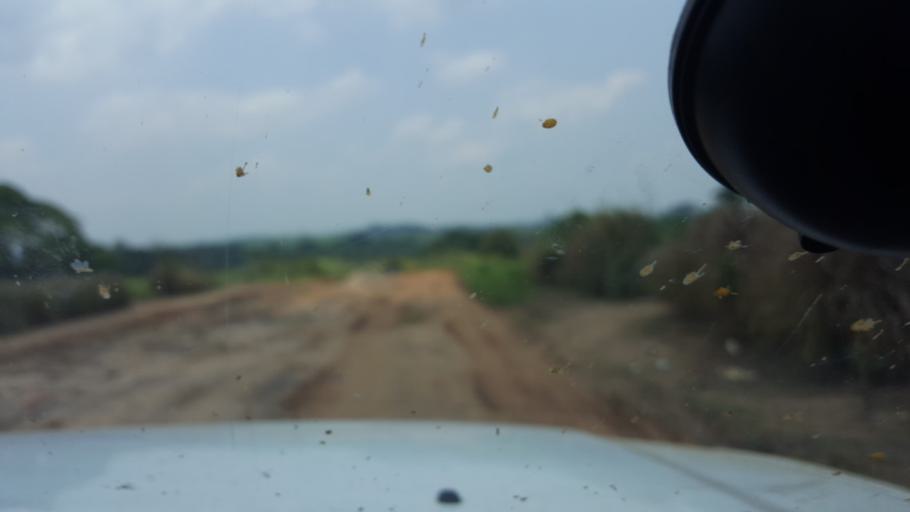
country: CD
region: Bandundu
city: Mushie
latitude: -3.7433
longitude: 16.6545
